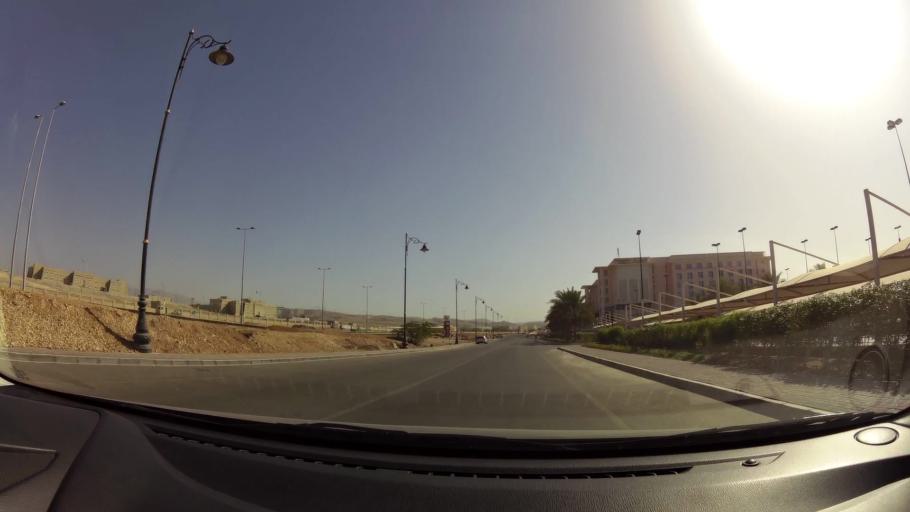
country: OM
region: Muhafazat Masqat
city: Bawshar
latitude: 23.5776
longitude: 58.2937
